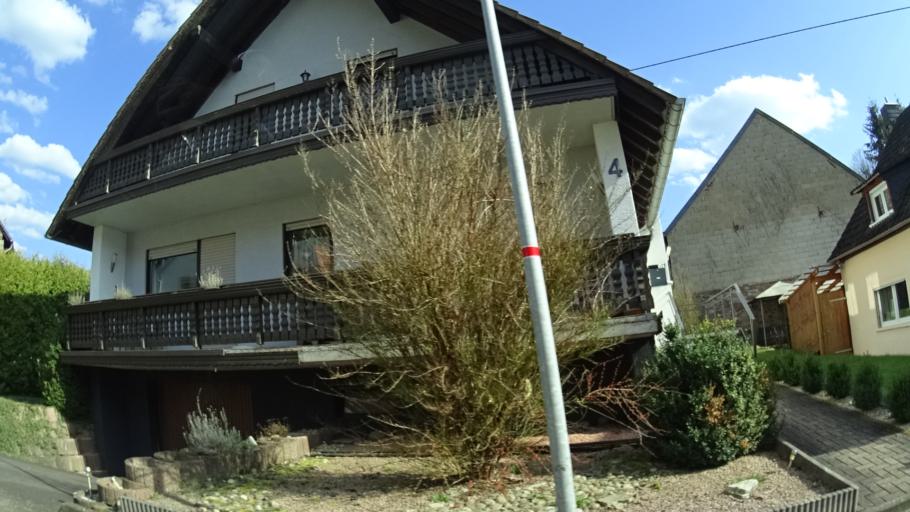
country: DE
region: Rheinland-Pfalz
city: Otzweiler
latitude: 49.7139
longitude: 7.5123
